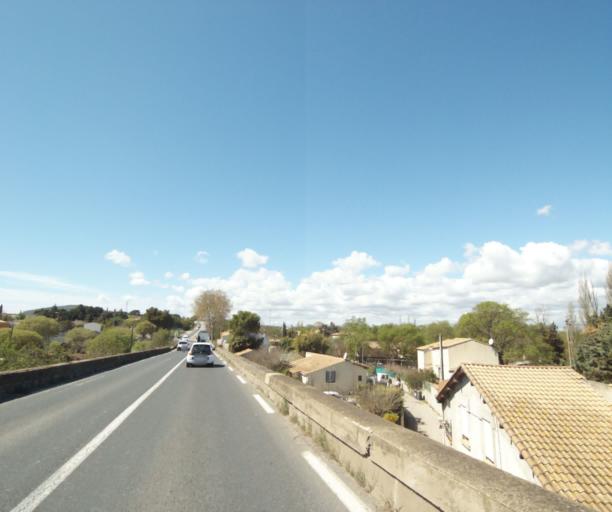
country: FR
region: Languedoc-Roussillon
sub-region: Departement de l'Herault
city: Villeneuve-les-Maguelone
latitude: 43.5551
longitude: 3.8463
